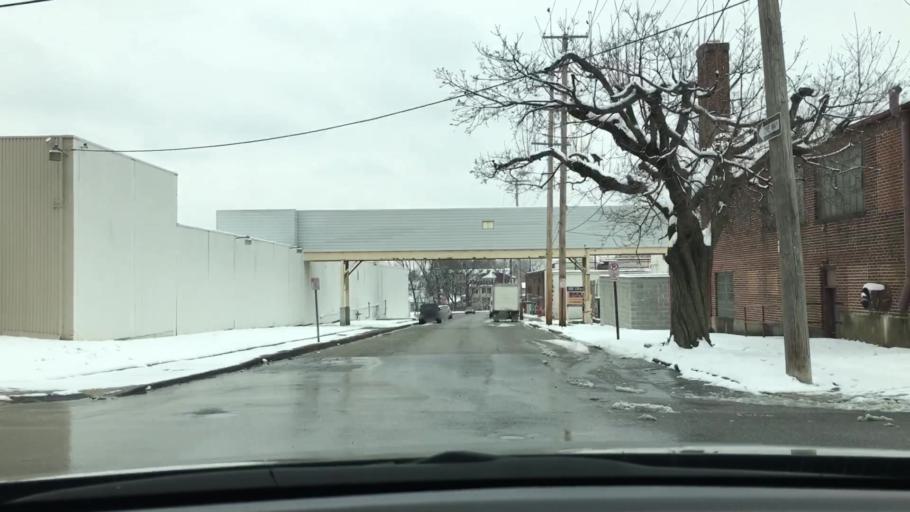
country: US
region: Pennsylvania
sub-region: York County
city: York
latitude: 39.9561
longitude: -76.7177
